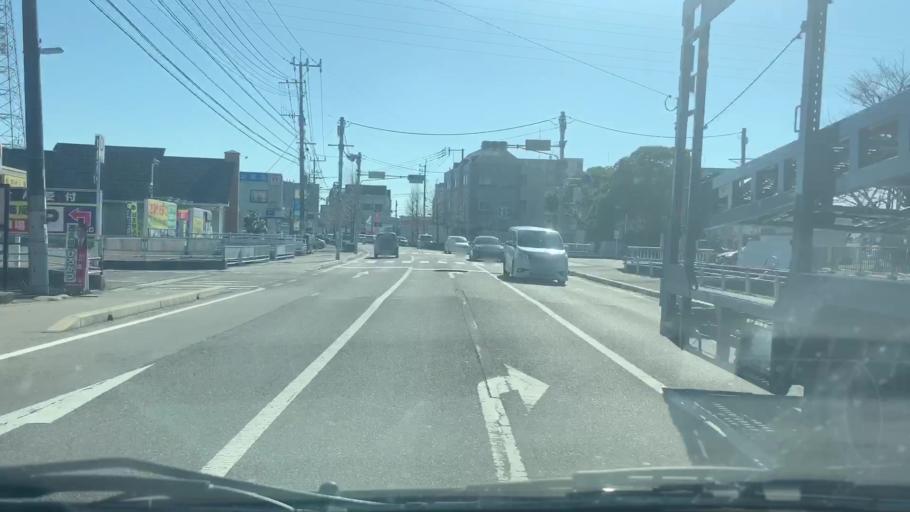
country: JP
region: Saga Prefecture
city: Saga-shi
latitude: 33.2837
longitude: 130.2686
